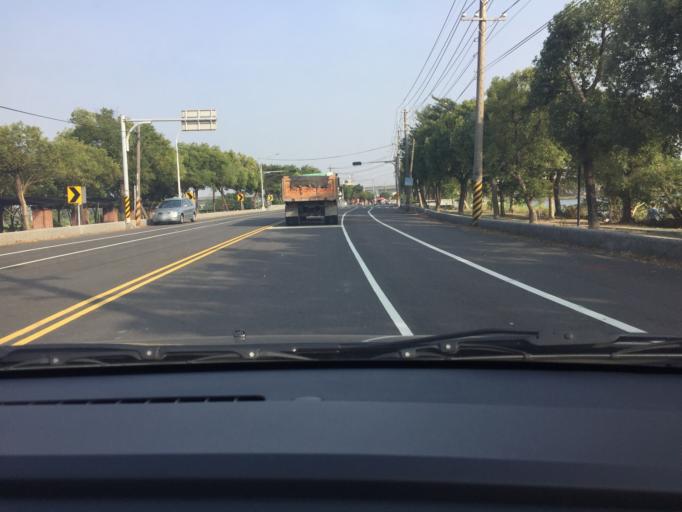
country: TW
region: Taiwan
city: Xinying
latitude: 23.1994
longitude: 120.2948
